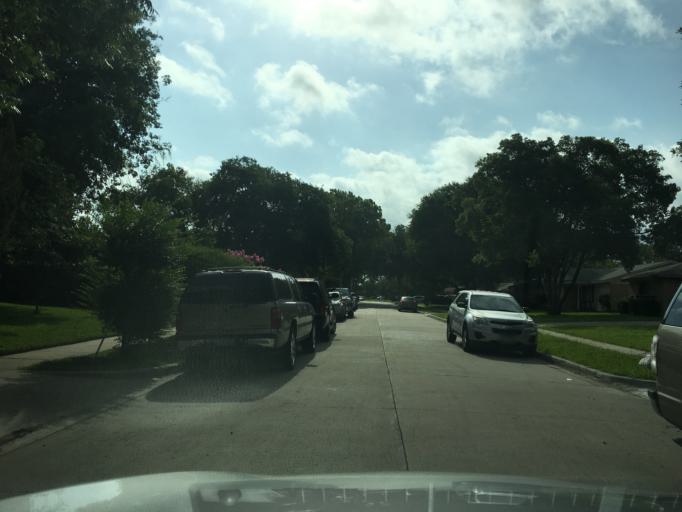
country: US
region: Texas
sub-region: Dallas County
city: Richardson
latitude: 32.9492
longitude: -96.7214
